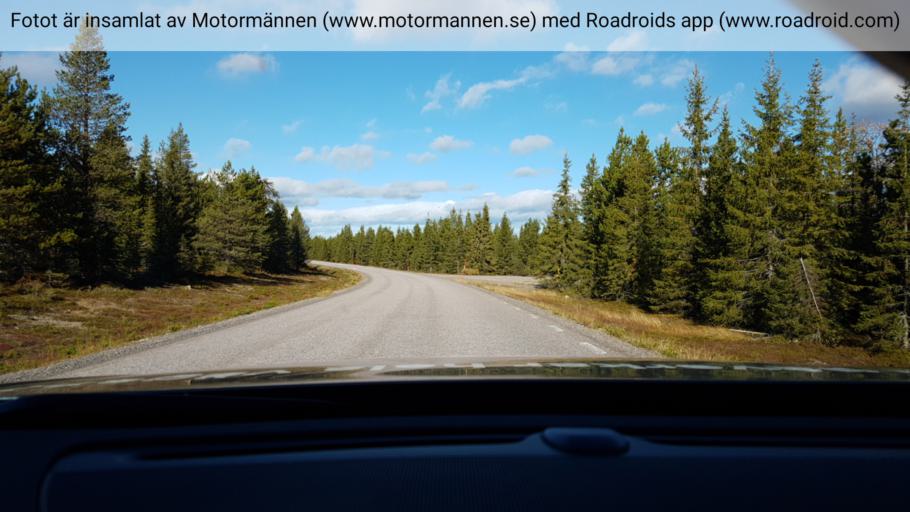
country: SE
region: Norrbotten
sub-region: Arjeplogs Kommun
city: Arjeplog
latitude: 65.8356
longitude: 18.4285
